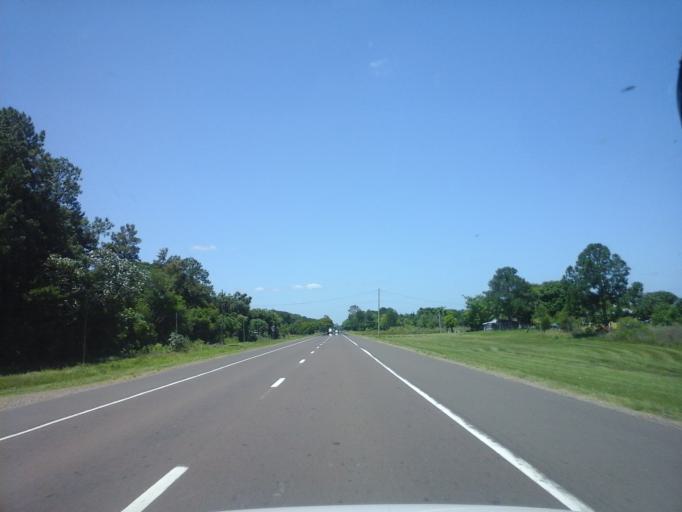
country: AR
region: Corrientes
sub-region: Departamento de San Cosme
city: San Cosme
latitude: -27.3783
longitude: -58.5231
